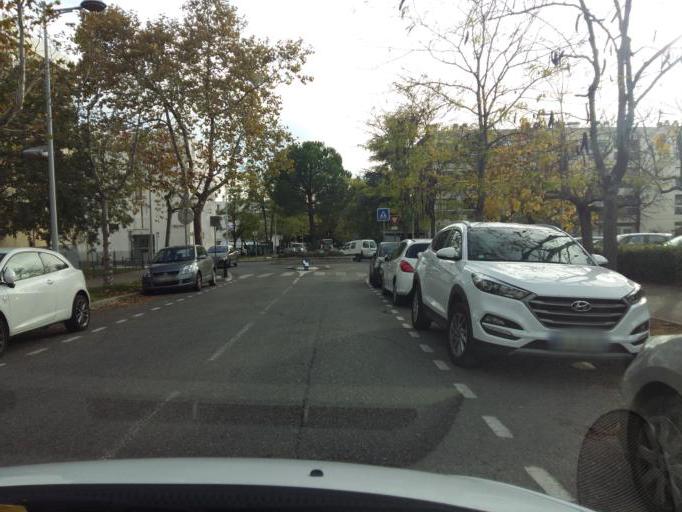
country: FR
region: Provence-Alpes-Cote d'Azur
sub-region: Departement des Bouches-du-Rhone
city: Aix-en-Provence
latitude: 43.5224
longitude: 5.4327
